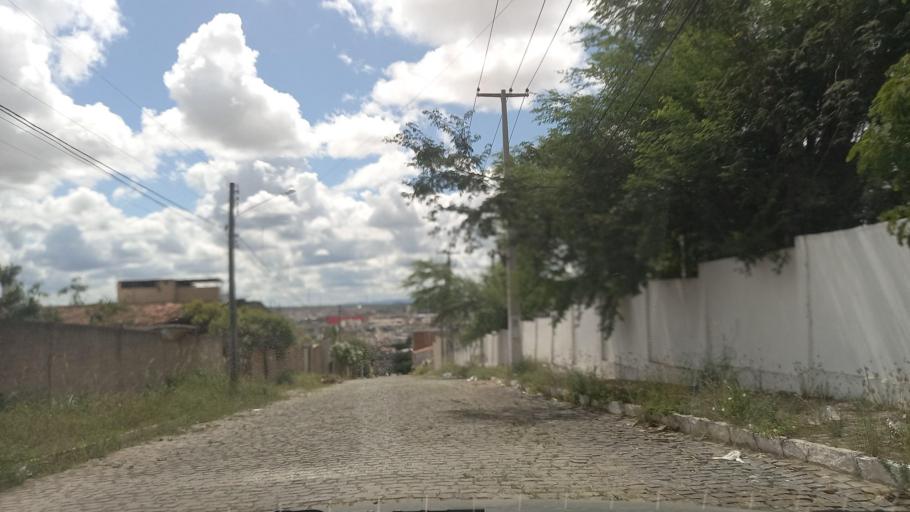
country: BR
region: Pernambuco
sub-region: Caruaru
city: Caruaru
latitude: -8.3007
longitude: -35.9797
